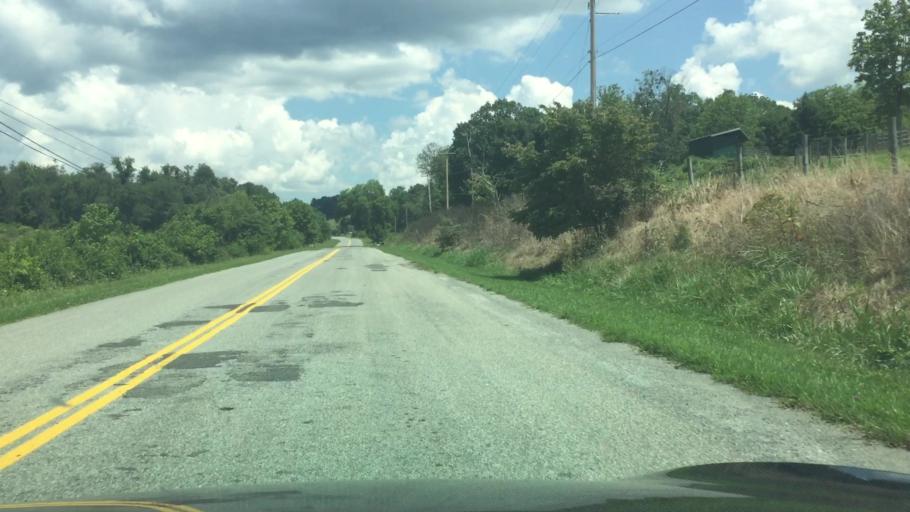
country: US
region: Virginia
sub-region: Pulaski County
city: Pulaski
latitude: 36.9792
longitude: -80.8313
